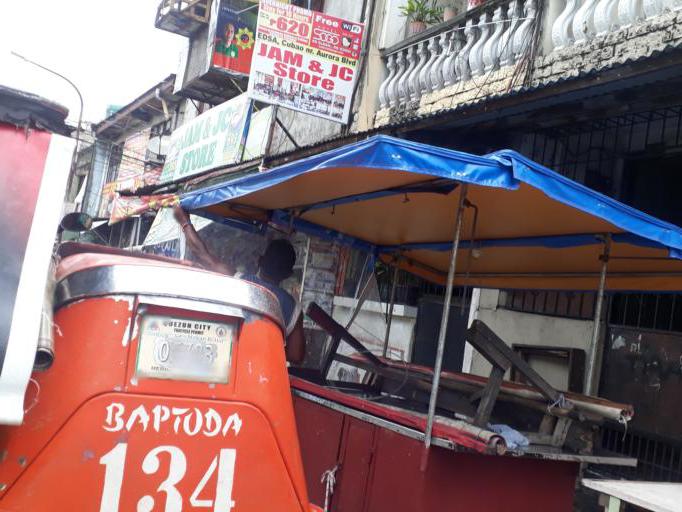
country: PH
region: Metro Manila
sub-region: San Juan
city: San Juan
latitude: 14.6181
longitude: 121.0490
